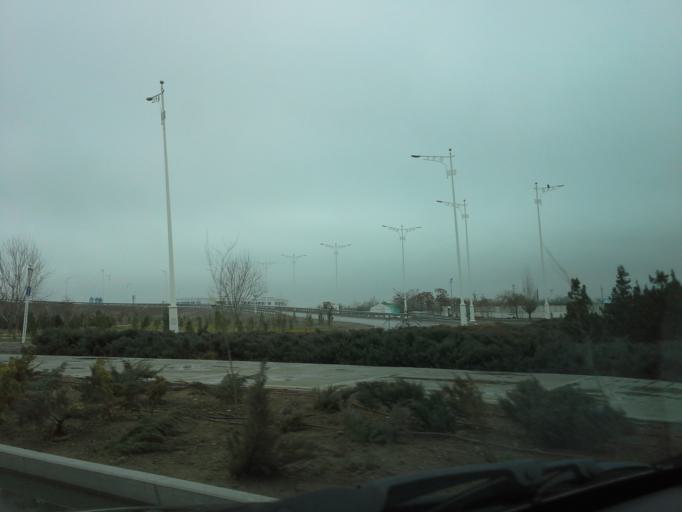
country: TM
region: Ahal
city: Ashgabat
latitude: 37.9614
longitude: 58.4168
